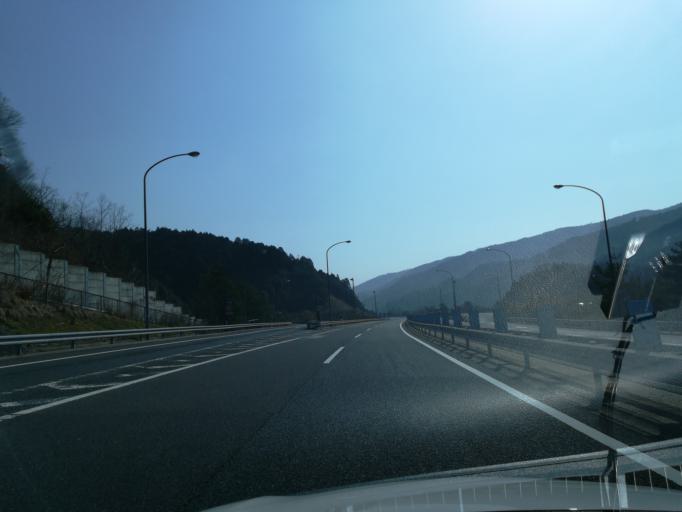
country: JP
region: Tokushima
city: Ikedacho
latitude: 34.0060
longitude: 133.7043
